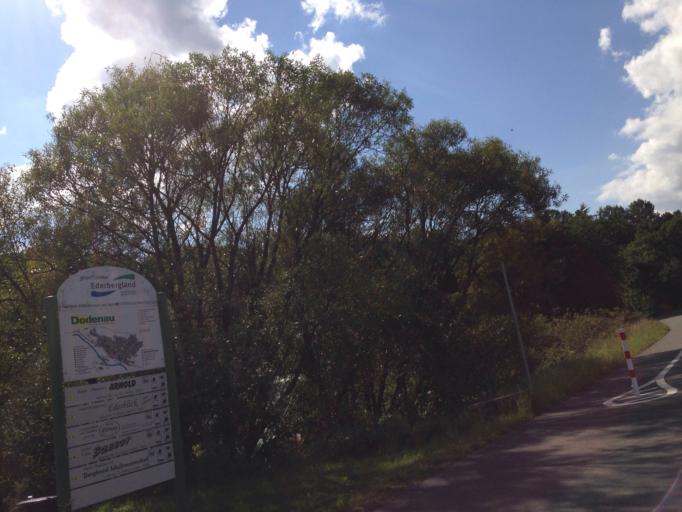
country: DE
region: Hesse
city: Hatzfeld
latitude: 51.0223
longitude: 8.5882
